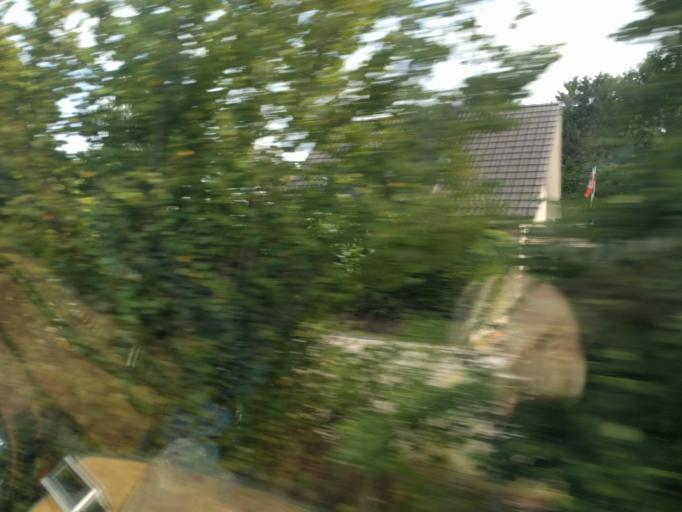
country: DE
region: Schleswig-Holstein
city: Stapelfeld
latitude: 53.6225
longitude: 10.1749
